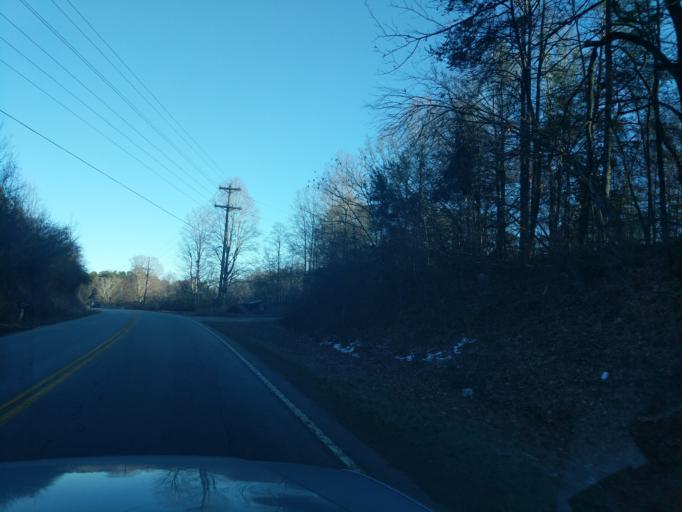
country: US
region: South Carolina
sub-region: Oconee County
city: Westminster
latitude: 34.6886
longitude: -83.1704
